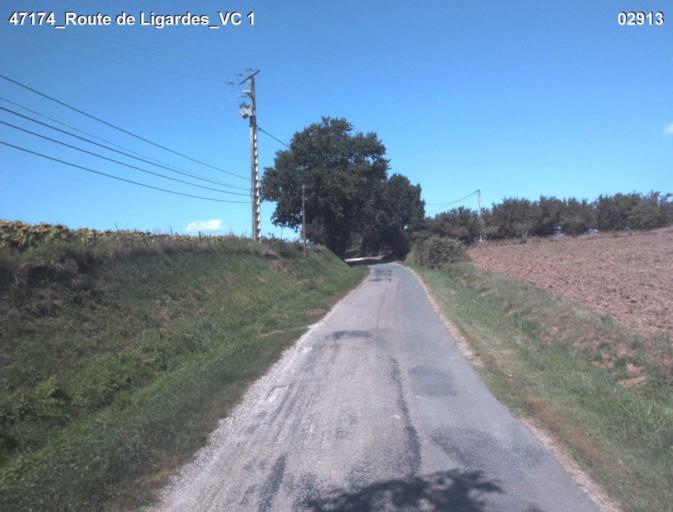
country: FR
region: Midi-Pyrenees
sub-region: Departement du Gers
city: Condom
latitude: 44.0326
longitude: 0.3862
